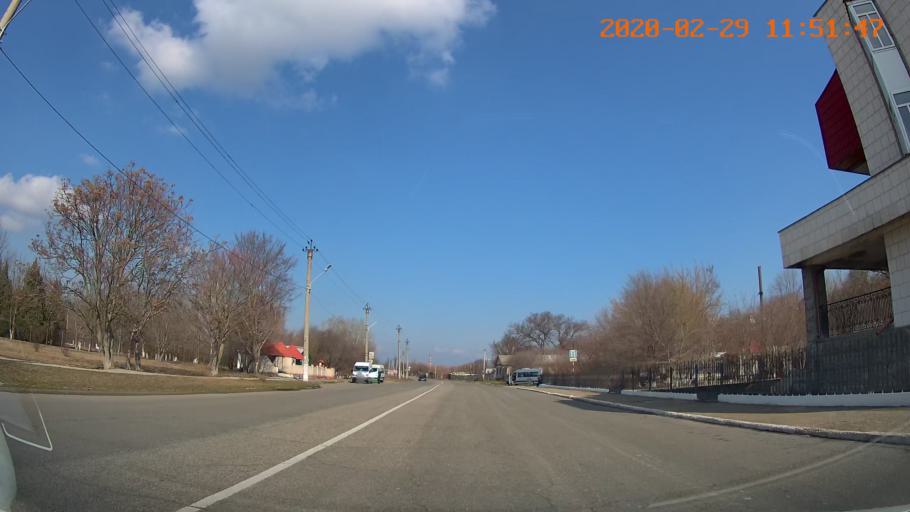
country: MD
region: Telenesti
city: Ribnita
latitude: 47.7666
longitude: 28.9907
